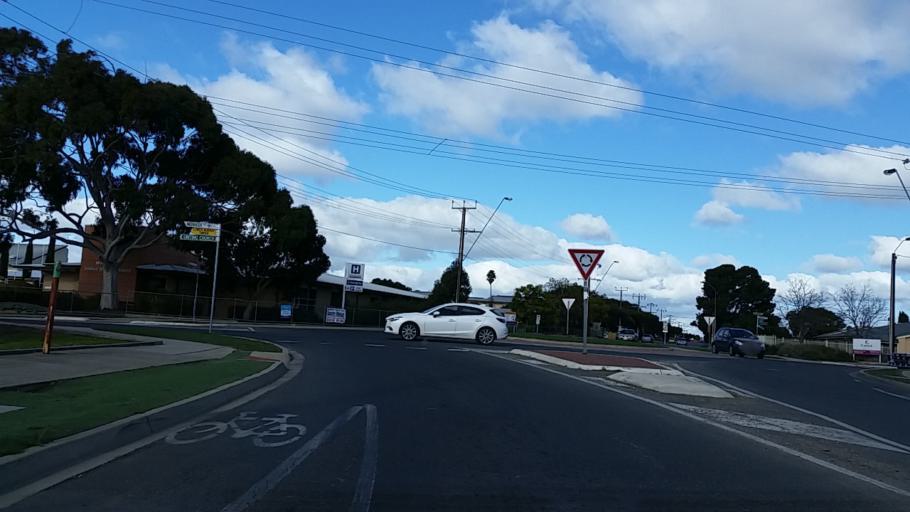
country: AU
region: South Australia
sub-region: Murray Bridge
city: Murray Bridge
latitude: -35.1284
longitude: 139.2793
